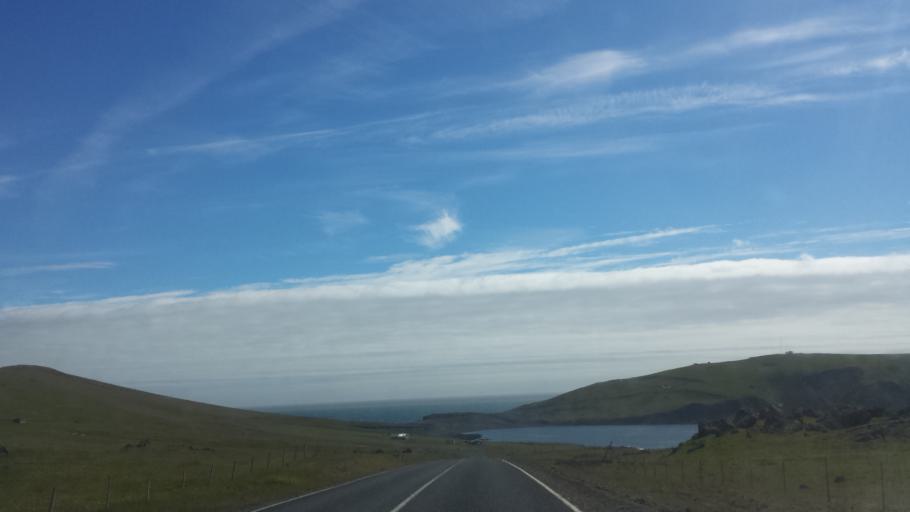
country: IS
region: South
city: Vestmannaeyjar
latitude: 63.4182
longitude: -20.2887
